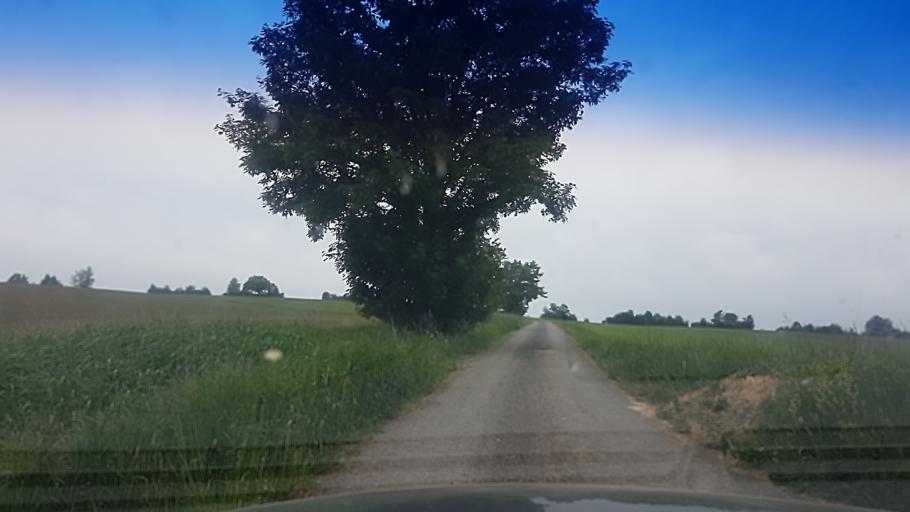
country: DE
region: Bavaria
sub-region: Upper Franconia
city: Buttenheim
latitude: 49.8125
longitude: 11.0435
